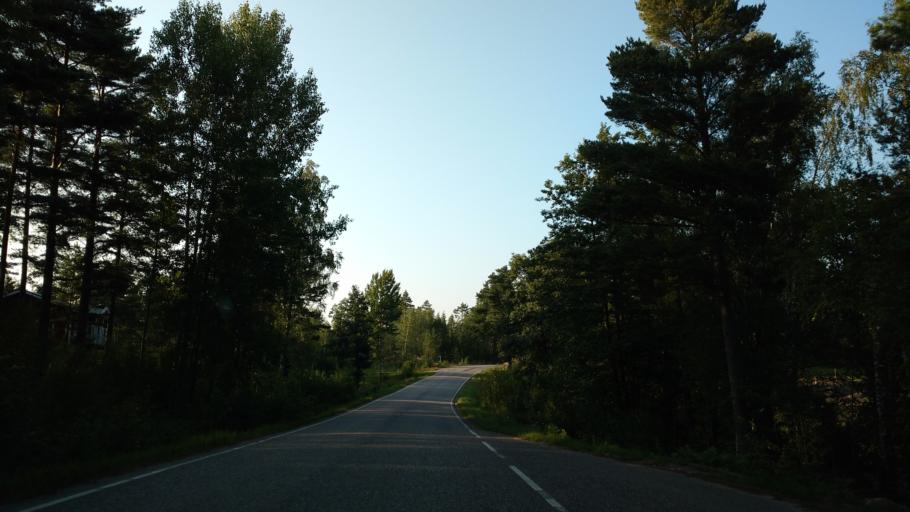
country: FI
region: Varsinais-Suomi
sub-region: Aboland-Turunmaa
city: Dragsfjaerd
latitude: 60.0019
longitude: 22.4537
